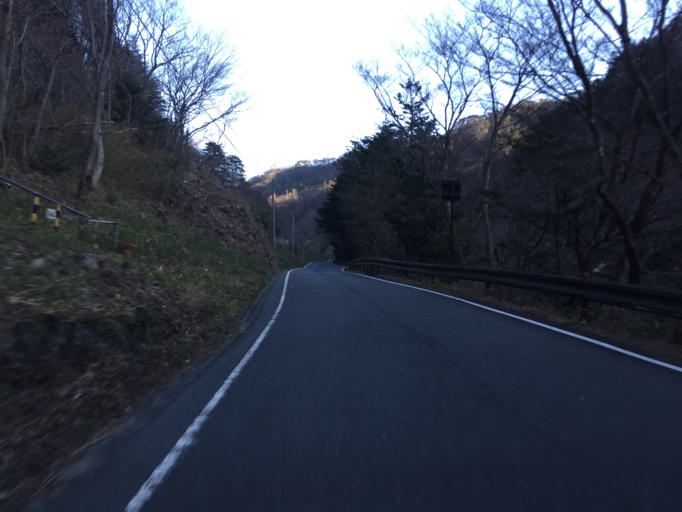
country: JP
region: Fukushima
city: Iwaki
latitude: 37.1926
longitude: 140.7938
